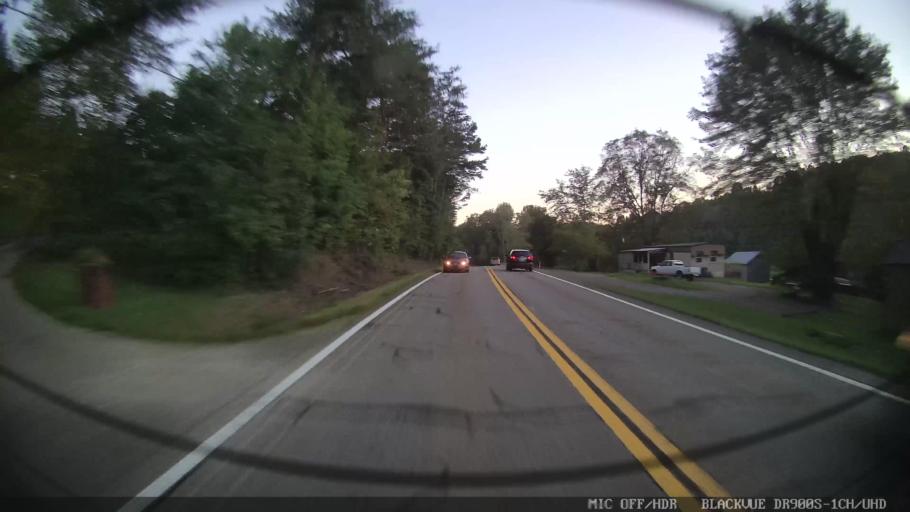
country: US
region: Georgia
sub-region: Gilmer County
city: Ellijay
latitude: 34.7184
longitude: -84.5026
